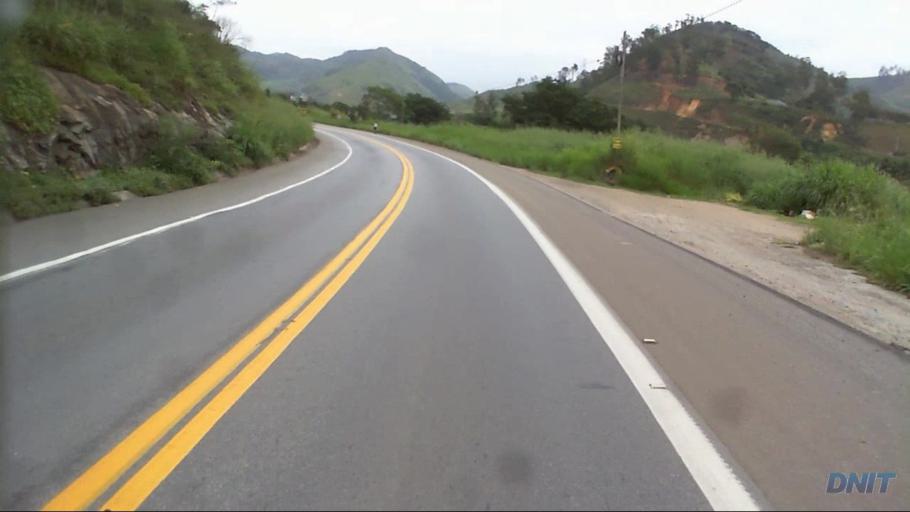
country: BR
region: Minas Gerais
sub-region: Timoteo
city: Timoteo
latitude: -19.5546
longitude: -42.7102
